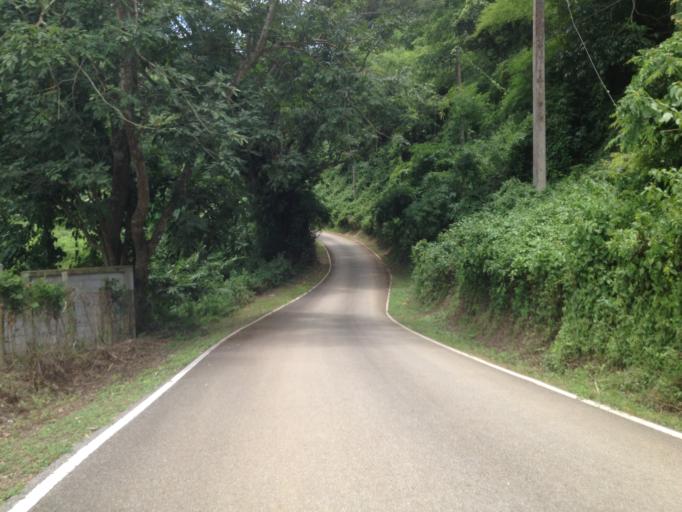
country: TH
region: Chiang Mai
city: Hang Dong
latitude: 18.7236
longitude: 98.8319
